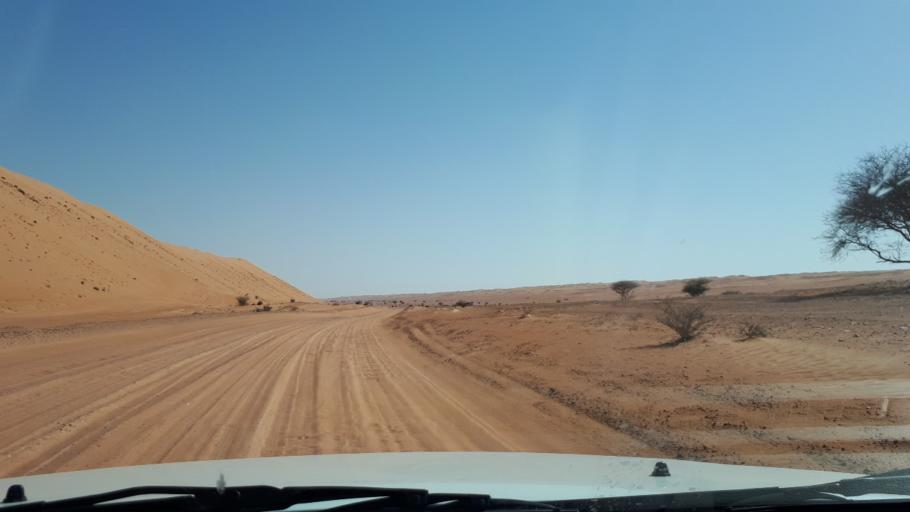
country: OM
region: Ash Sharqiyah
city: Badiyah
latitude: 22.4609
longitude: 58.7418
